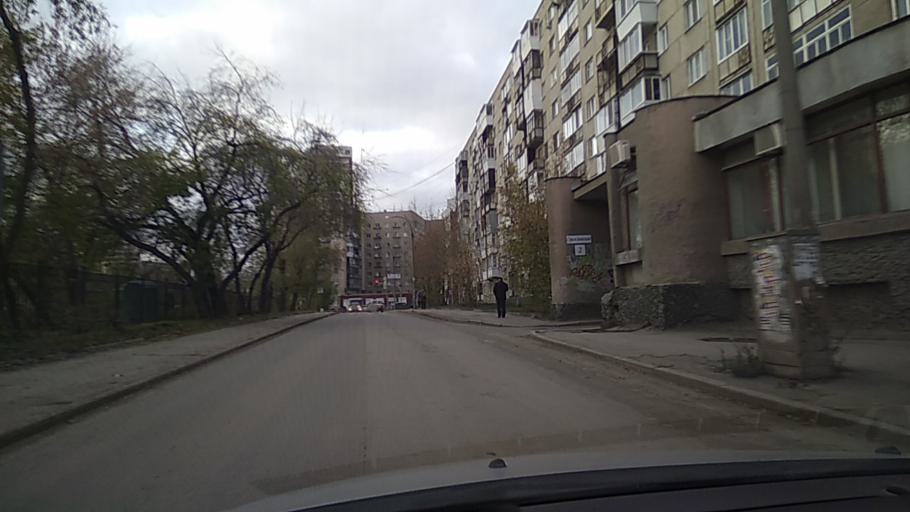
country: RU
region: Sverdlovsk
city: Yekaterinburg
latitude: 56.8526
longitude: 60.5838
